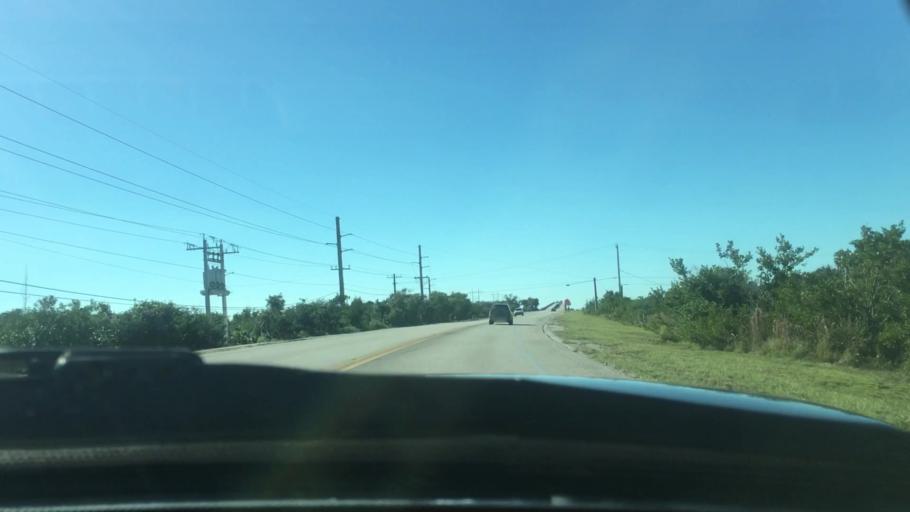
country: US
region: Florida
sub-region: Monroe County
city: Big Pine Key
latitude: 24.6603
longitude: -81.4186
